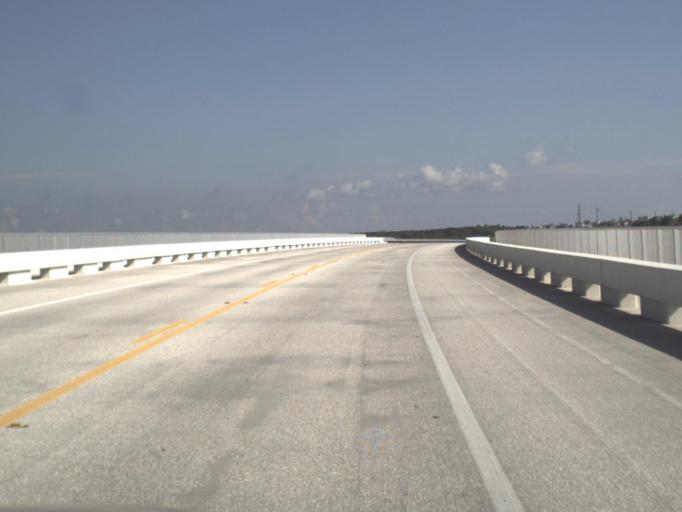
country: US
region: Florida
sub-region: Flagler County
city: Palm Coast
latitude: 29.6793
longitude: -81.2206
